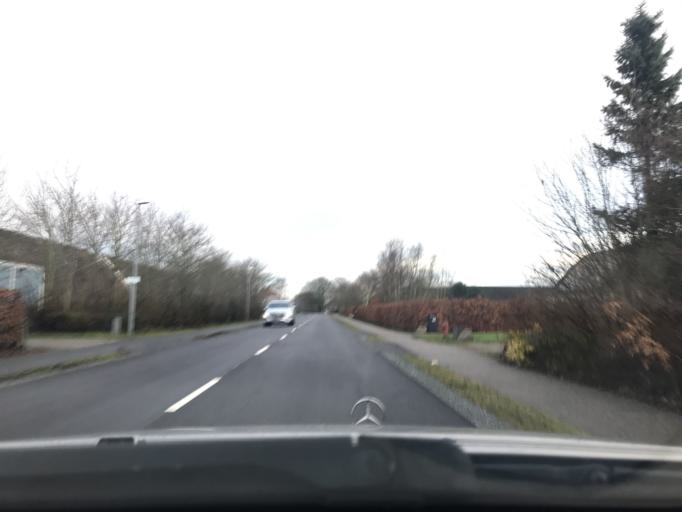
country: DK
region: South Denmark
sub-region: Esbjerg Kommune
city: Ribe
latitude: 55.3162
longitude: 8.7323
